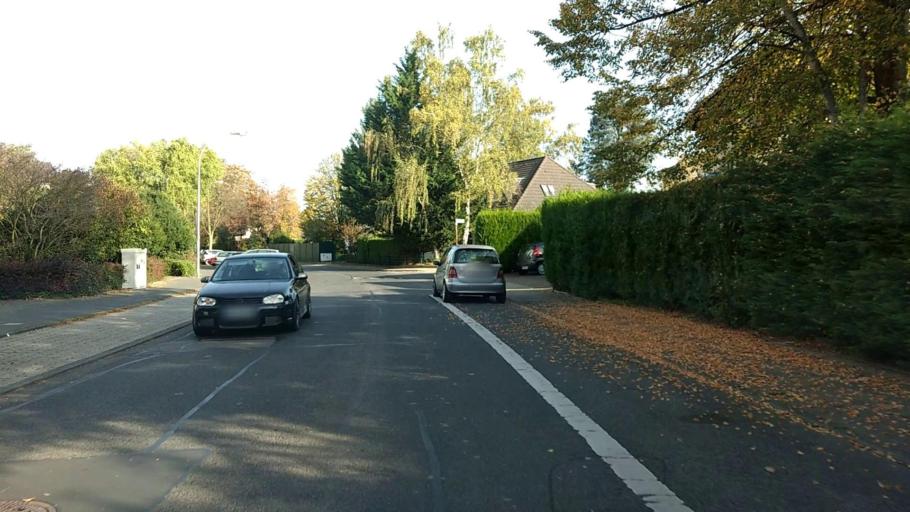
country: DE
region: North Rhine-Westphalia
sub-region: Regierungsbezirk Koln
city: Kerpen
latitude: 50.9072
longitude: 6.6826
